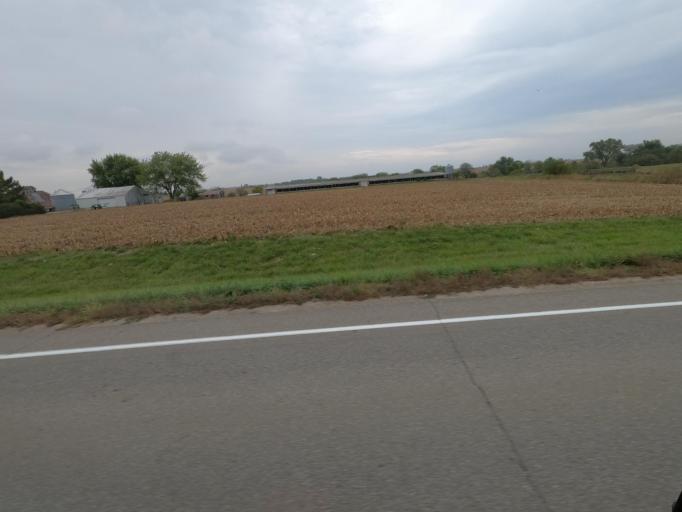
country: US
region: Iowa
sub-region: Van Buren County
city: Keosauqua
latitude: 40.8134
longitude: -91.8167
